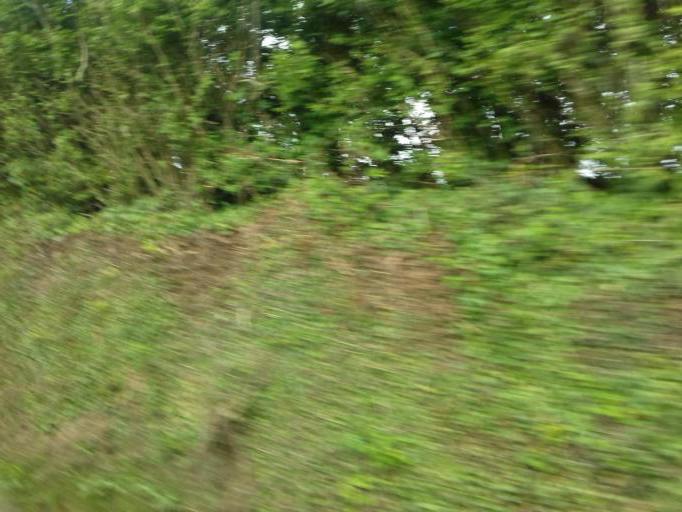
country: IE
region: Munster
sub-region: Waterford
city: Dunmore East
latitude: 52.2044
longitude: -6.8555
